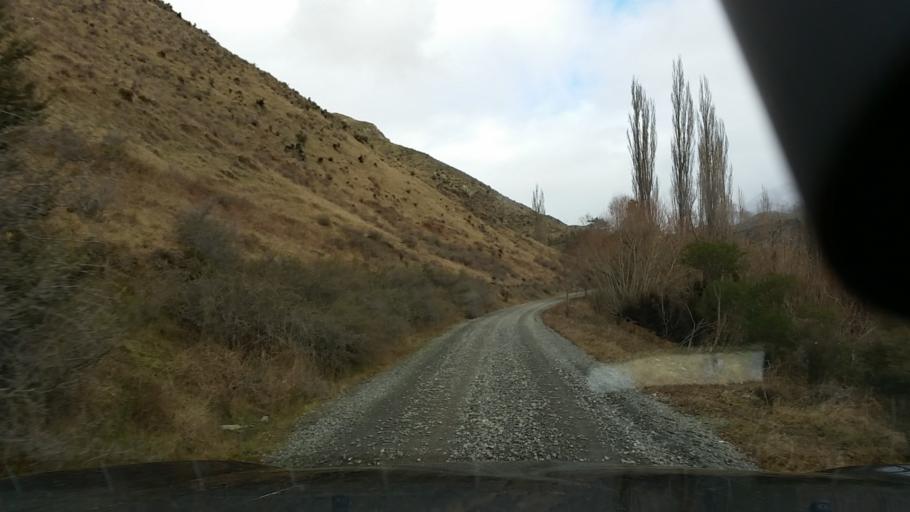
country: NZ
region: Tasman
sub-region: Tasman District
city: Brightwater
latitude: -41.7445
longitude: 173.4135
